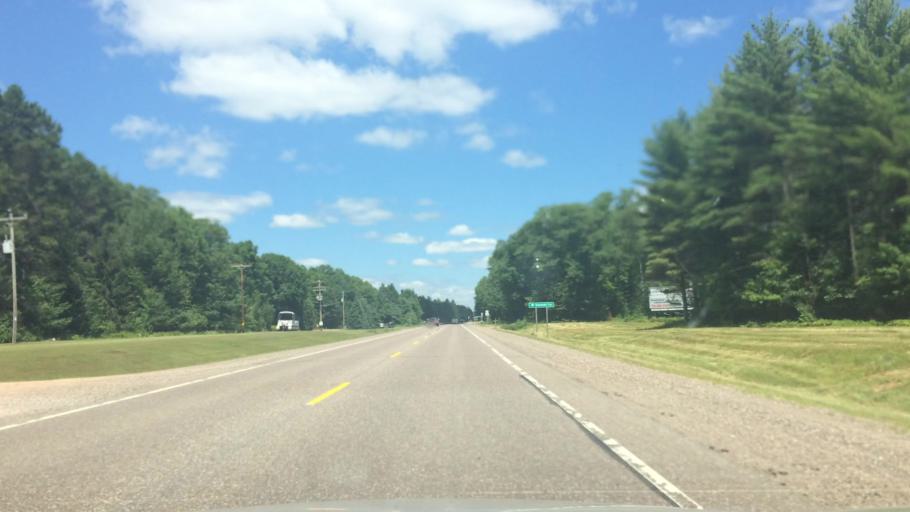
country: US
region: Wisconsin
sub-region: Vilas County
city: Lac du Flambeau
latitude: 45.9776
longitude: -89.6991
